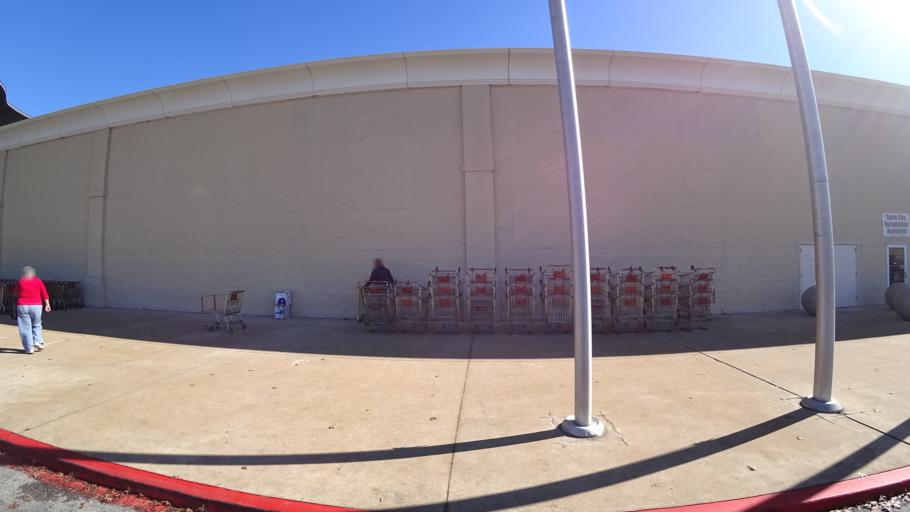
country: US
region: Texas
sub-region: Travis County
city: Wells Branch
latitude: 30.4226
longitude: -97.7005
